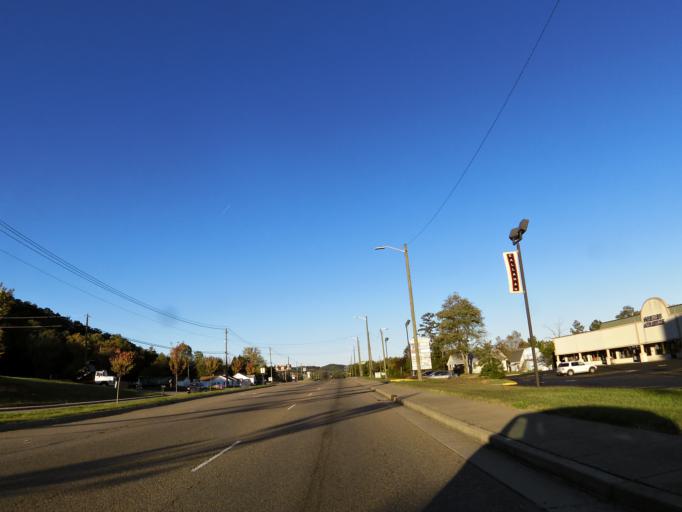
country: US
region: Tennessee
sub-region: Knox County
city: Knoxville
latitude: 36.0193
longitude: -84.0065
